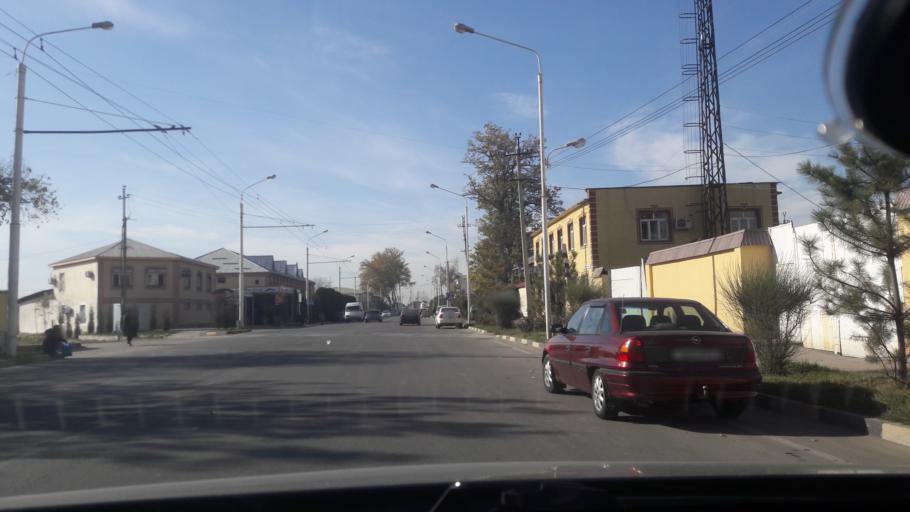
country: TJ
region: Dushanbe
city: Dushanbe
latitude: 38.5576
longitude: 68.7931
